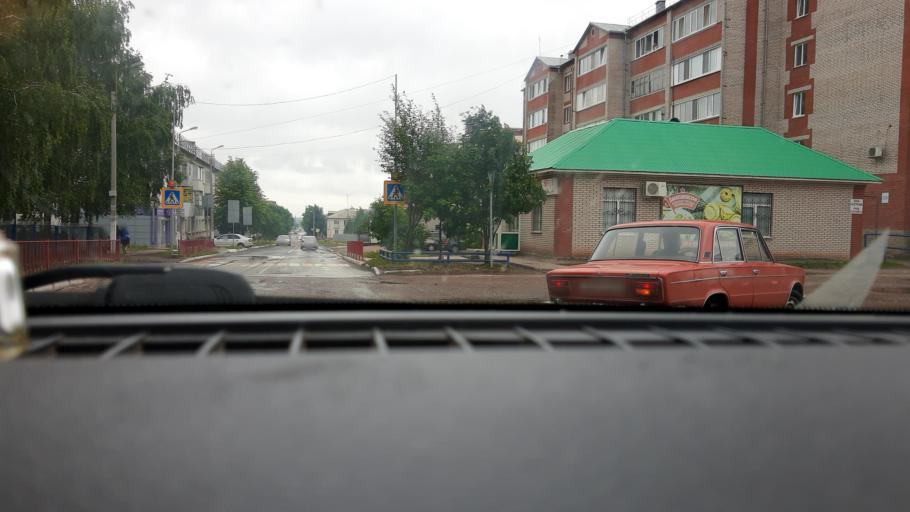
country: RU
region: Bashkortostan
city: Priyutovo
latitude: 53.9052
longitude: 53.9337
